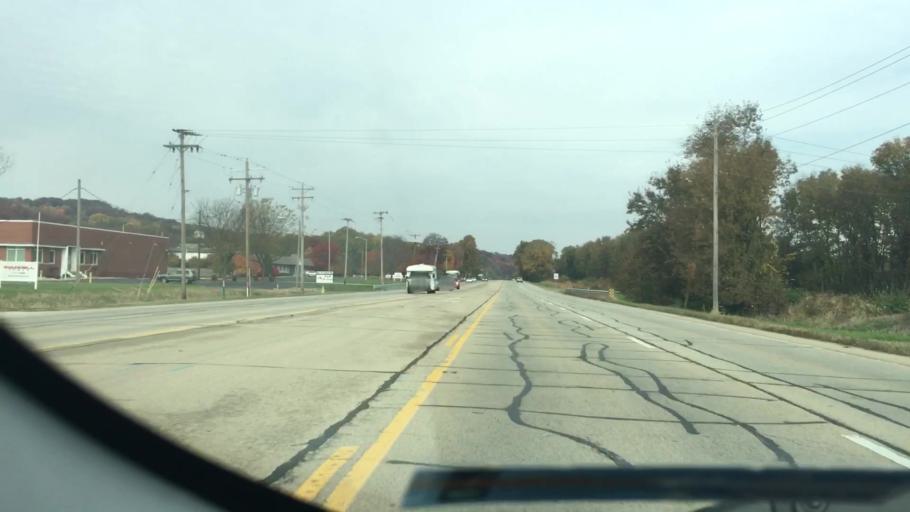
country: US
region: Illinois
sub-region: Peoria County
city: Peoria Heights
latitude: 40.7645
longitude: -89.5687
